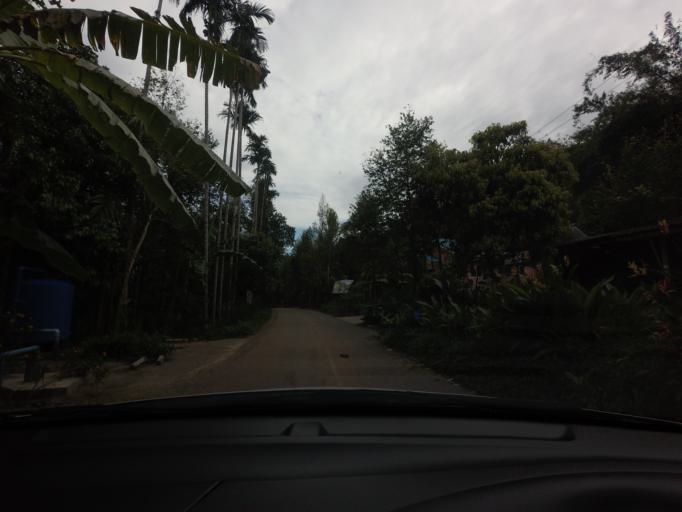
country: TH
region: Nakhon Nayok
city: Nakhon Nayok
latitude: 14.3353
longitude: 101.2855
